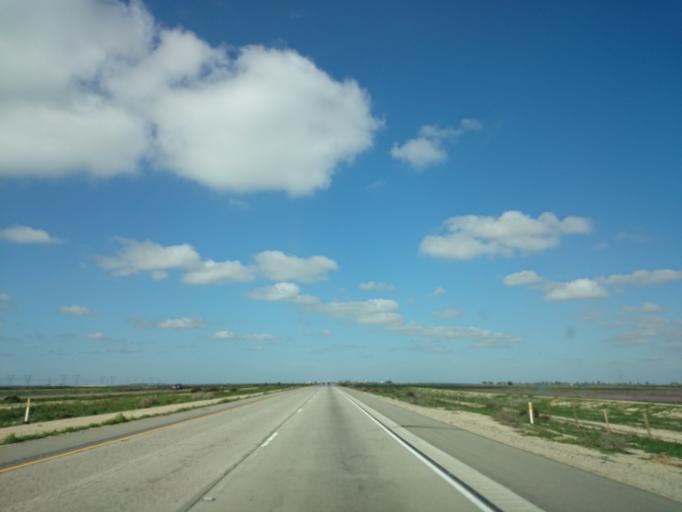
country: US
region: California
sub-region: Kern County
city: Rosedale
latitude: 35.3343
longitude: -119.3066
